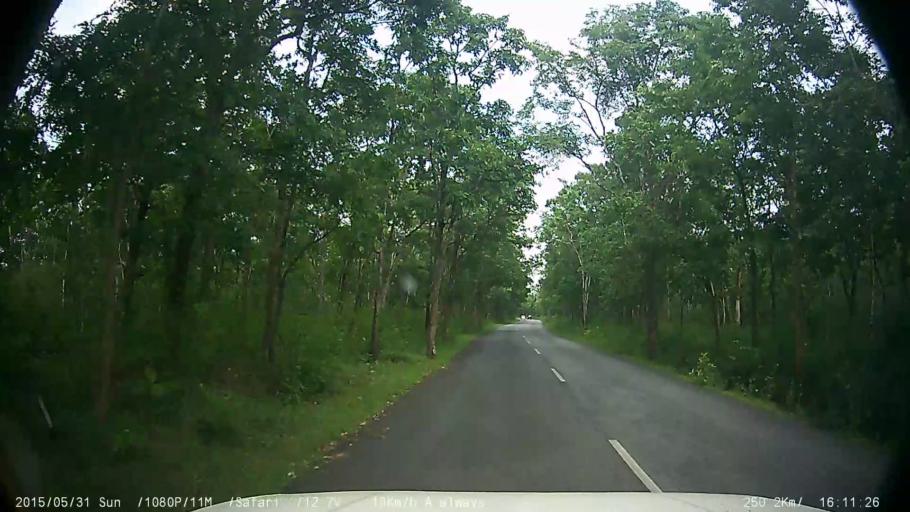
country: IN
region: Tamil Nadu
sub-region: Nilgiri
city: Masinigudi
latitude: 11.7288
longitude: 76.4448
